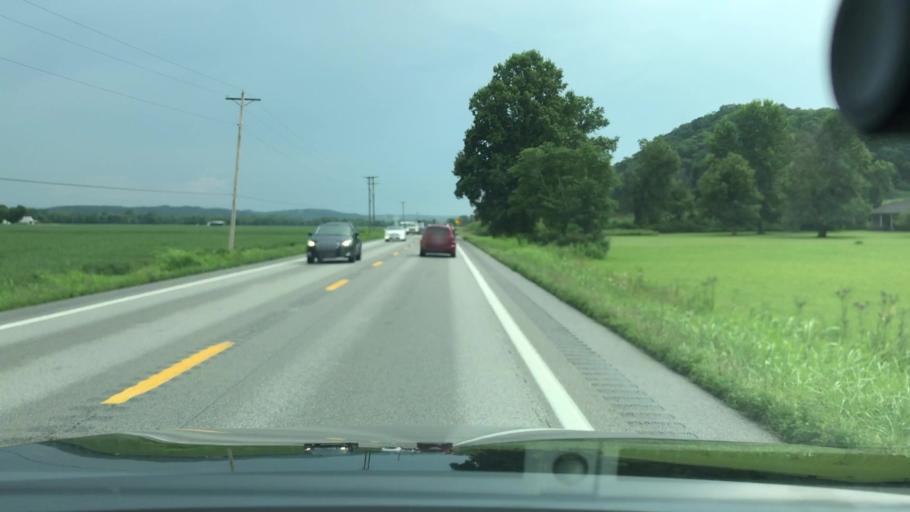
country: US
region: West Virginia
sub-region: Putnam County
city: Buffalo
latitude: 38.6722
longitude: -81.9664
